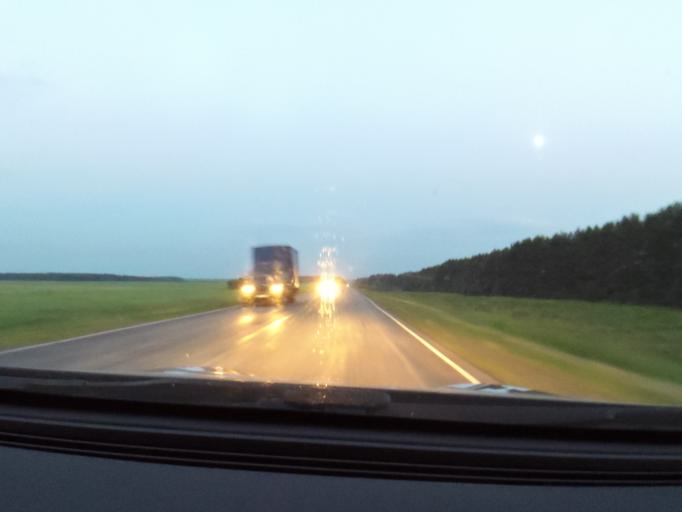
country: RU
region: Bashkortostan
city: Duvan
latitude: 56.1036
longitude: 58.0609
